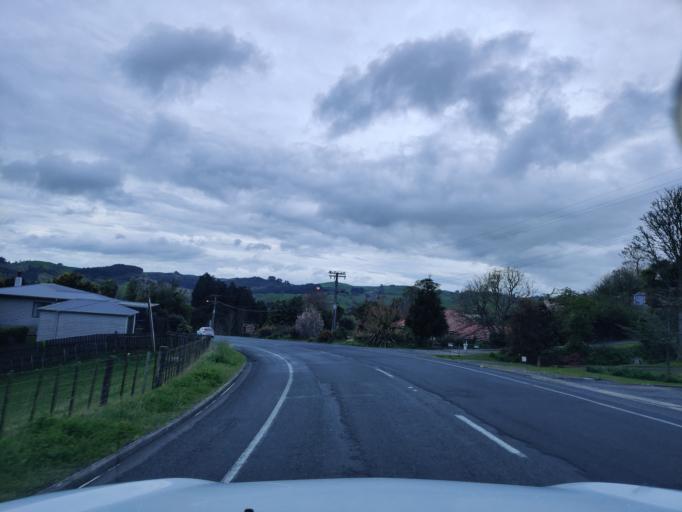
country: NZ
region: Waikato
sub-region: Otorohanga District
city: Otorohanga
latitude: -38.3479
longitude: 175.1672
